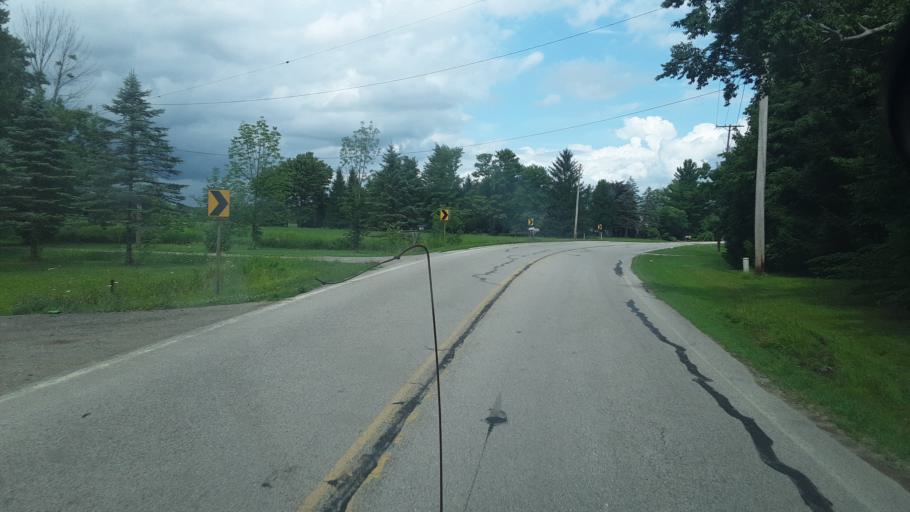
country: US
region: Ohio
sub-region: Ashtabula County
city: Jefferson
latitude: 41.7825
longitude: -80.7793
